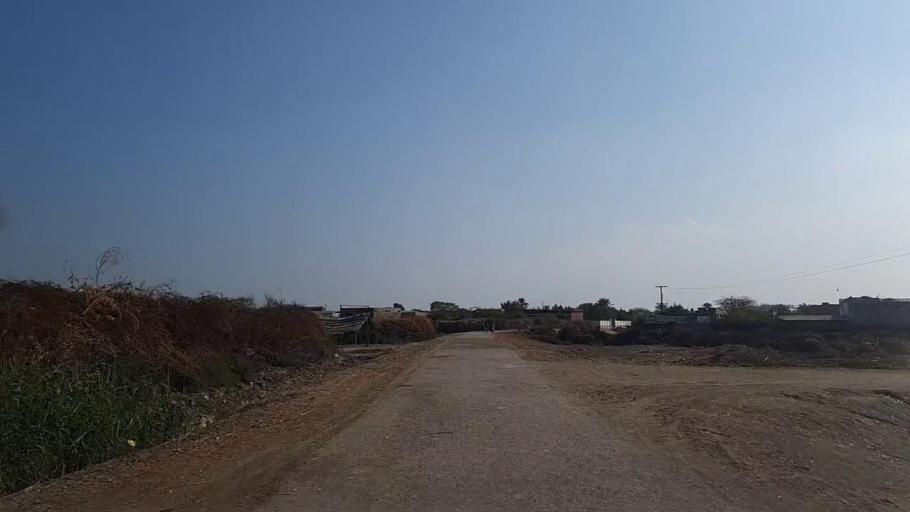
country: PK
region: Sindh
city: Jam Sahib
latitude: 26.2756
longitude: 68.5836
